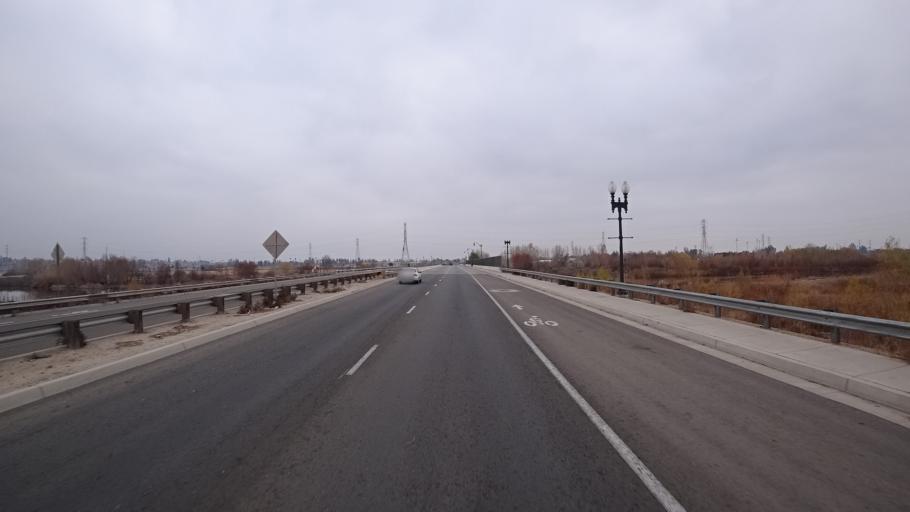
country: US
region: California
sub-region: Kern County
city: Oildale
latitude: 35.4033
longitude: -119.0204
